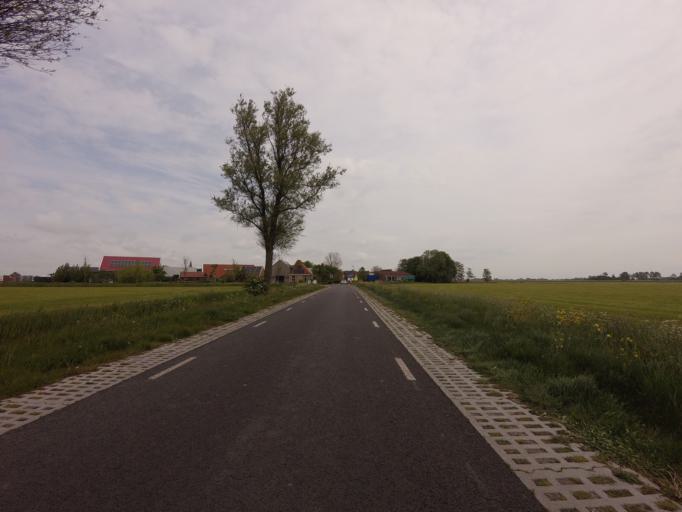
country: NL
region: Friesland
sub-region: Sudwest Fryslan
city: Bolsward
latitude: 53.0795
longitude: 5.4808
